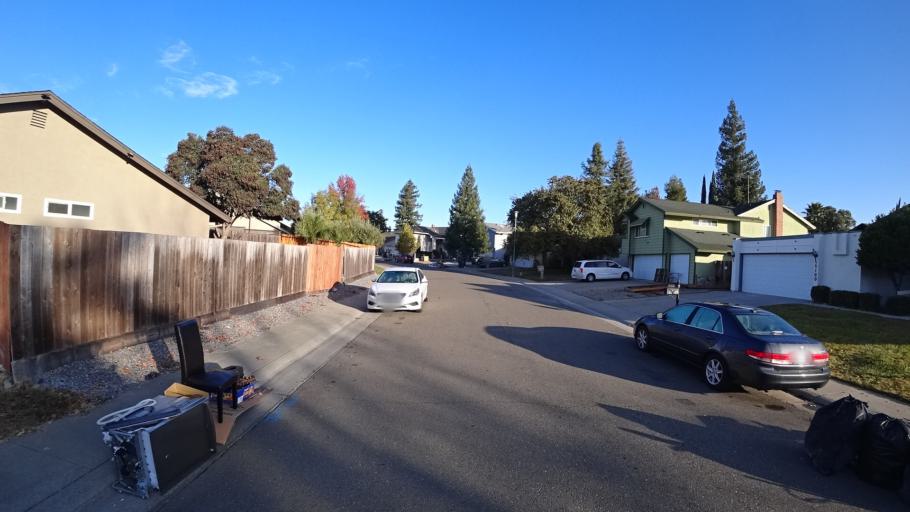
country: US
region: California
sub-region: Sacramento County
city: Citrus Heights
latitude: 38.6756
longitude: -121.3054
